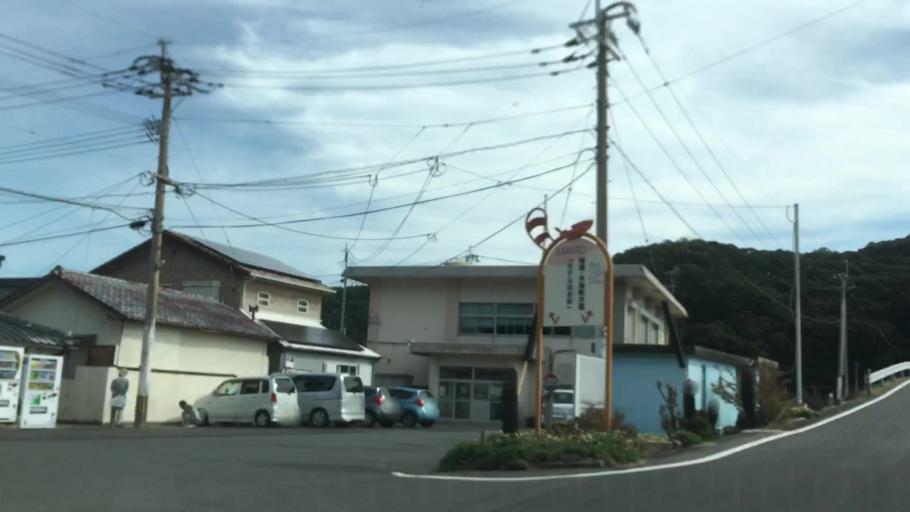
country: JP
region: Nagasaki
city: Sasebo
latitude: 33.0044
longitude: 129.5536
